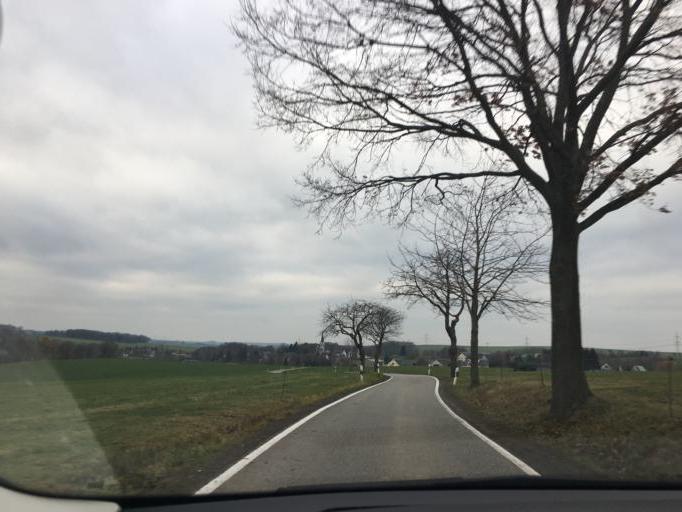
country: DE
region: Saxony
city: Niederfrohna
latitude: 50.8669
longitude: 12.7029
